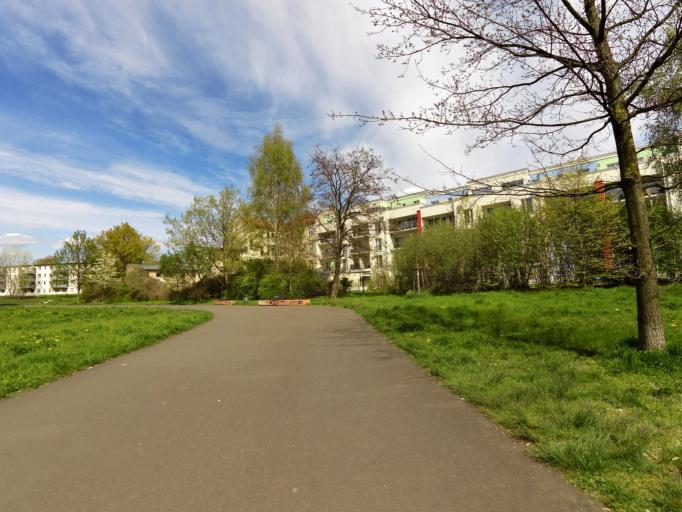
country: DE
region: Berlin
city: Baumschulenweg
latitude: 52.4642
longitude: 13.4790
